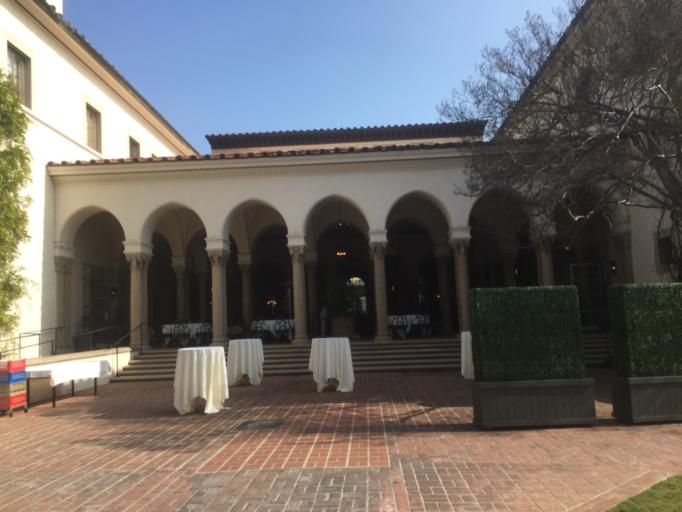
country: US
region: California
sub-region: Los Angeles County
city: San Marino
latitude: 34.1369
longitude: -118.1222
